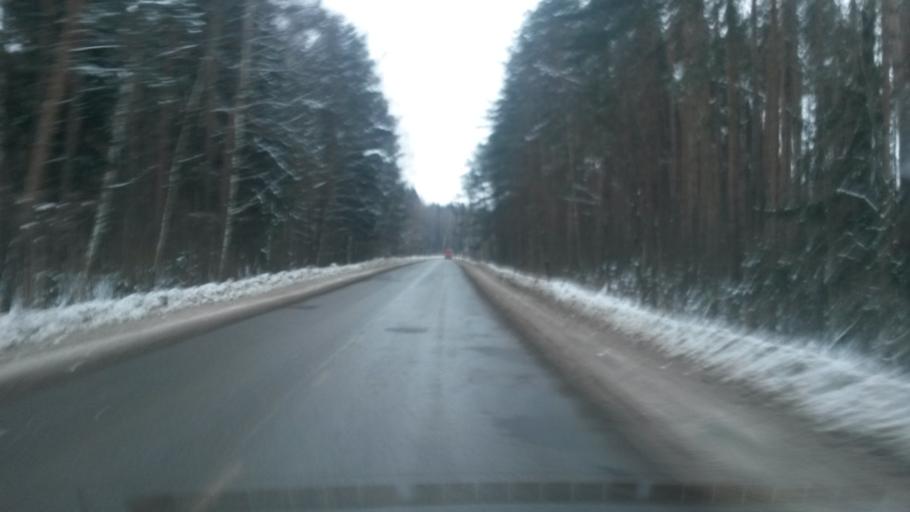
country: RU
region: Ivanovo
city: Kokhma
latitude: 56.9700
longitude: 41.0868
